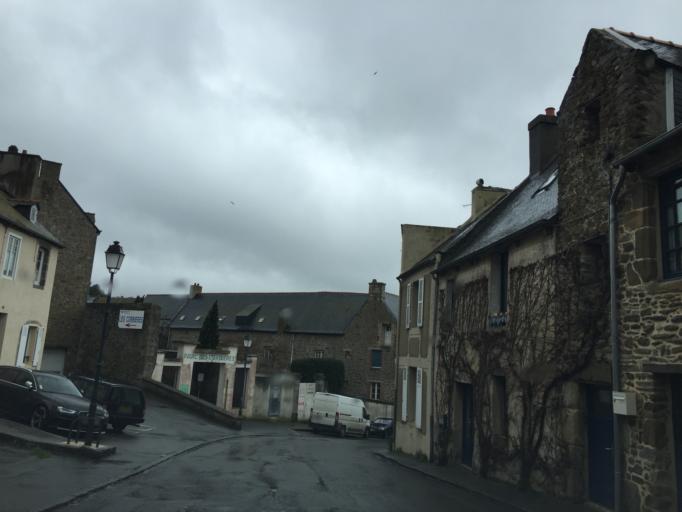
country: FR
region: Brittany
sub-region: Departement d'Ille-et-Vilaine
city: Saint-Malo
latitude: 48.6343
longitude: -2.0198
